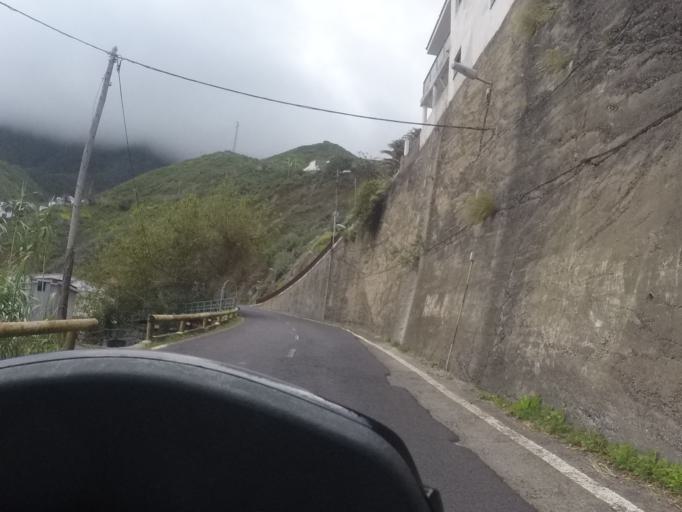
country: ES
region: Canary Islands
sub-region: Provincia de Santa Cruz de Tenerife
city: Santa Cruz de Tenerife
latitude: 28.5604
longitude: -16.2167
